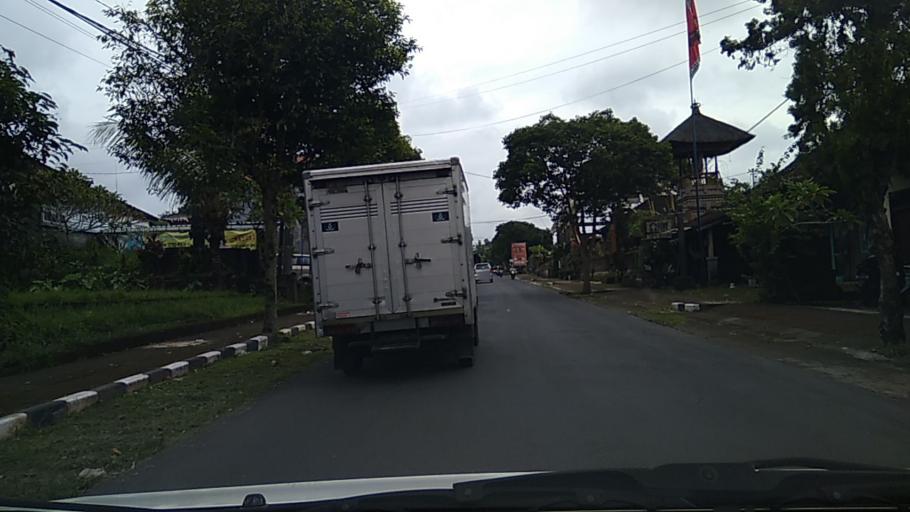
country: ID
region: Bali
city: Brahmana
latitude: -8.4881
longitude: 115.2101
